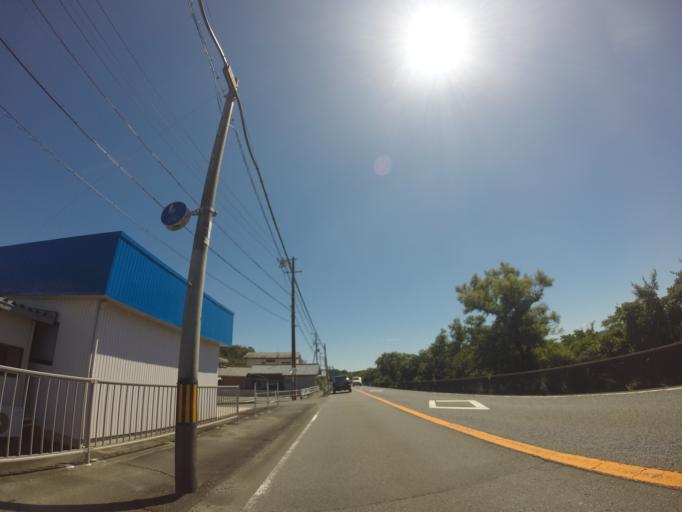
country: JP
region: Shizuoka
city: Kanaya
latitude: 34.8524
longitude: 138.1395
